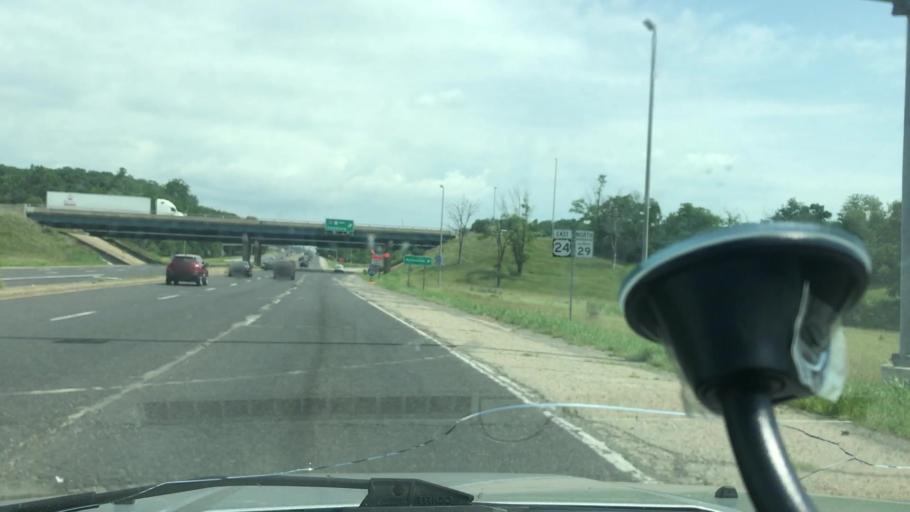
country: US
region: Illinois
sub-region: Tazewell County
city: North Pekin
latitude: 40.6286
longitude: -89.6140
